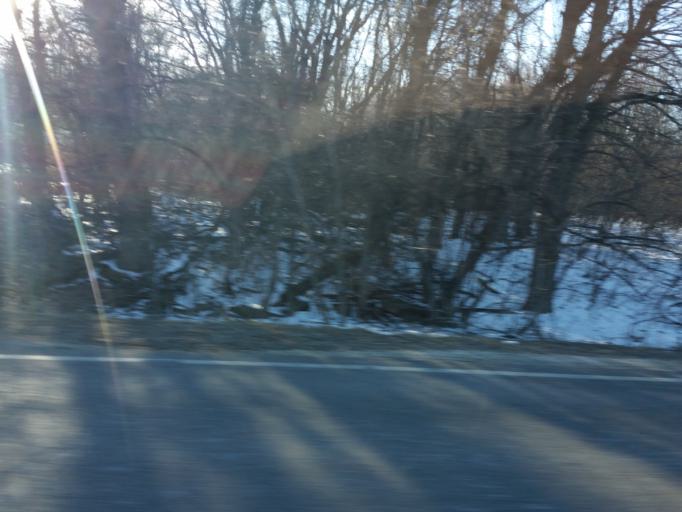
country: US
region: Minnesota
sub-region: Dakota County
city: Lakeville
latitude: 44.6445
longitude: -93.2530
